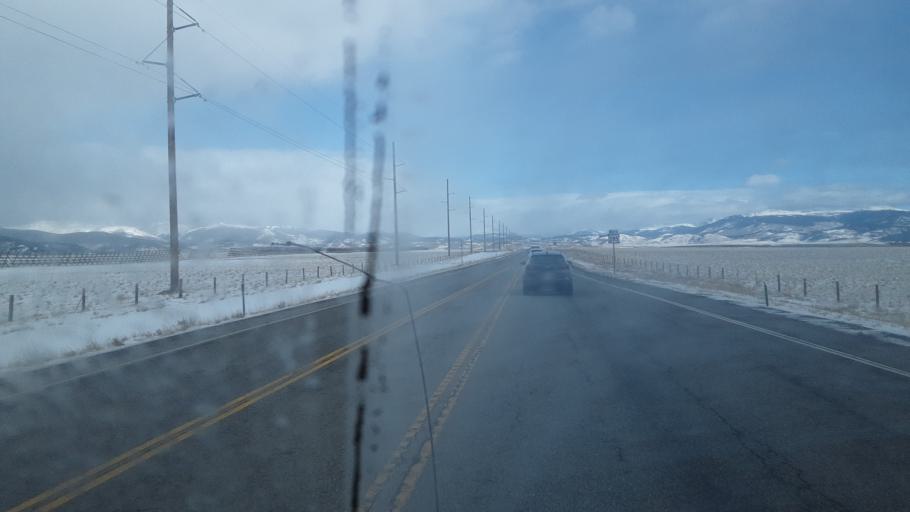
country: US
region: Colorado
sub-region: Park County
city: Fairplay
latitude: 39.3172
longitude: -105.8804
